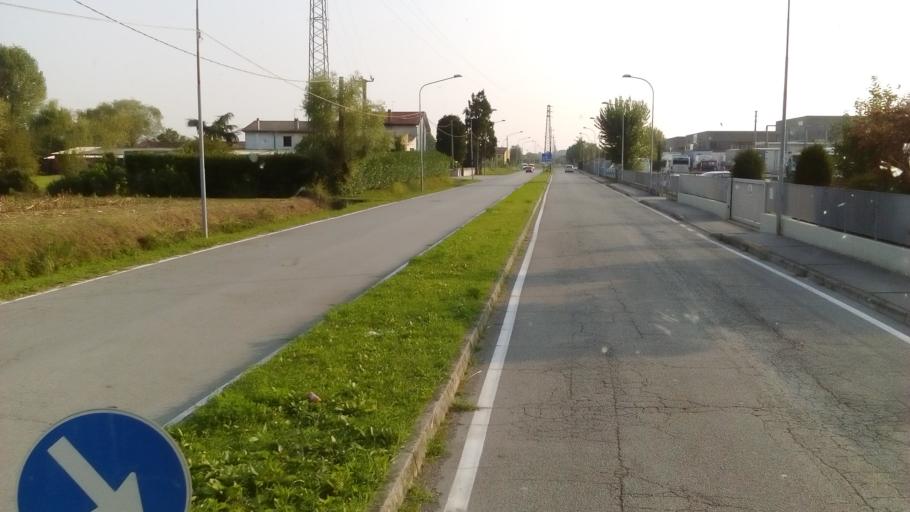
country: IT
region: Veneto
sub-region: Provincia di Padova
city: Mejaniga
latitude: 45.4748
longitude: 11.9064
